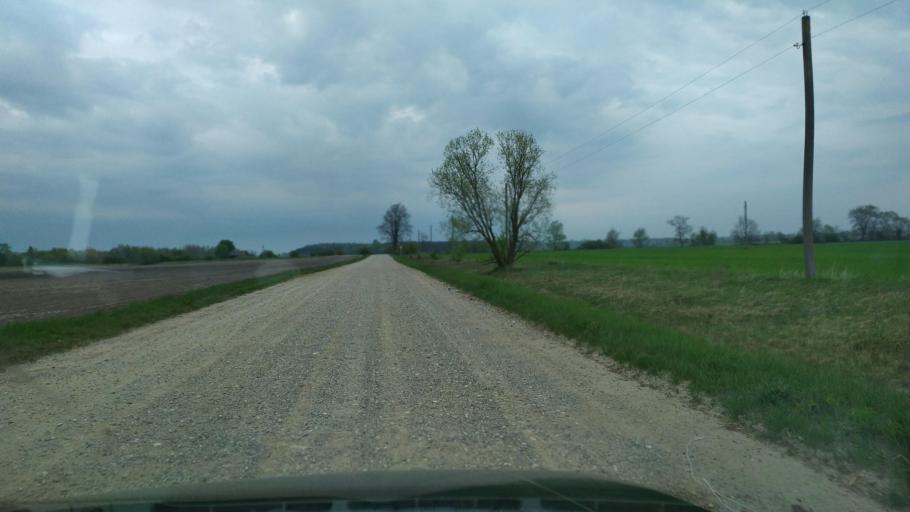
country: BY
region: Brest
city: Zhabinka
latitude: 52.1327
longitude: 24.0923
